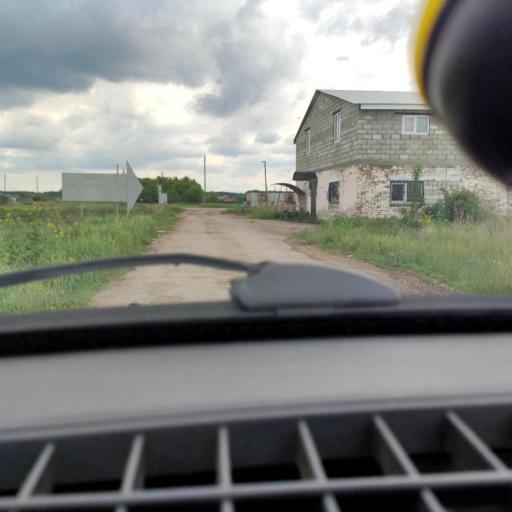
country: RU
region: Samara
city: Povolzhskiy
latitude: 53.6522
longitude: 49.6937
